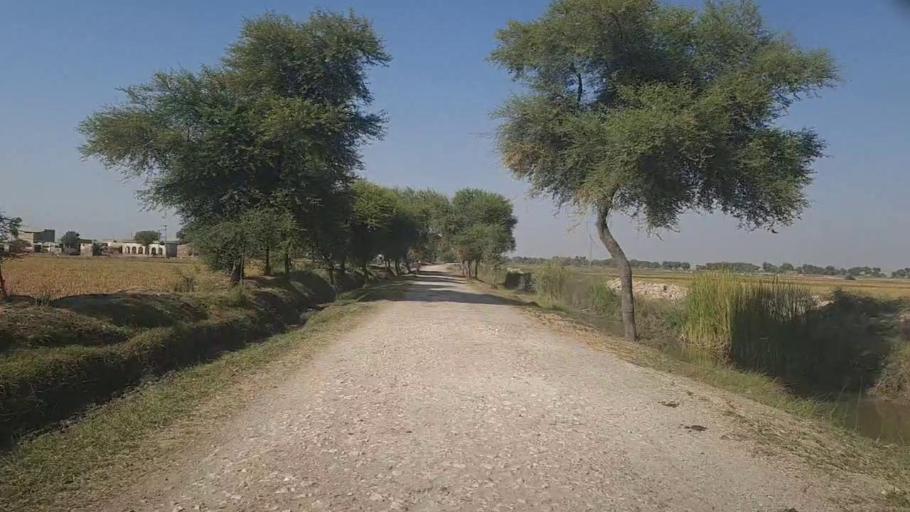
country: PK
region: Sindh
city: Thul
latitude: 28.3095
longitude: 68.7689
